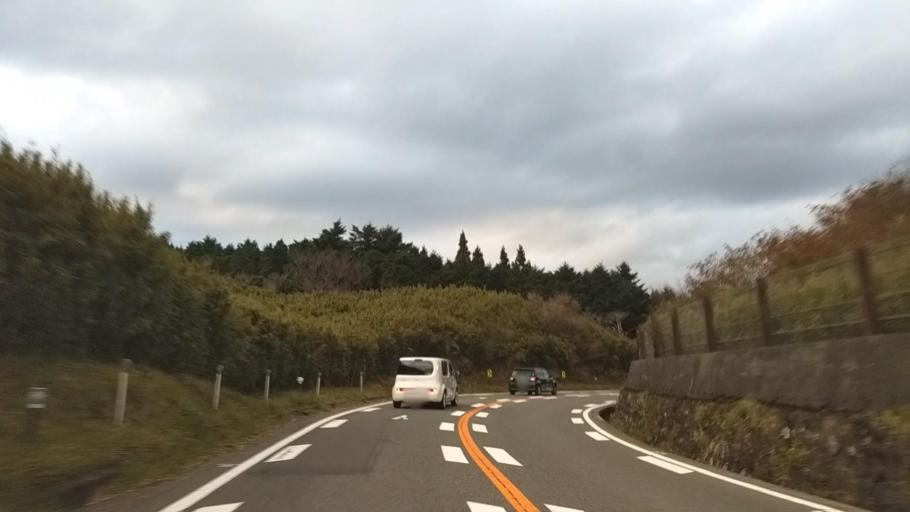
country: JP
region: Kanagawa
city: Yugawara
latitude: 35.1423
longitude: 139.0308
